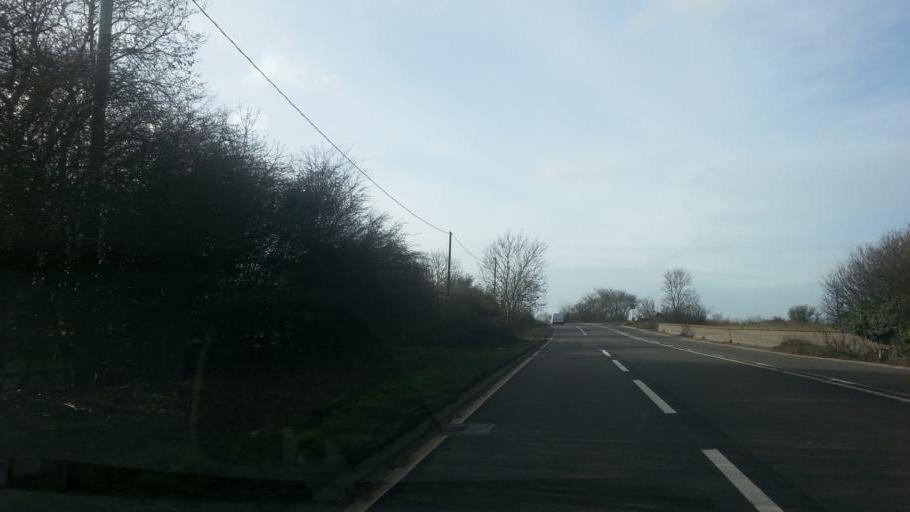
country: GB
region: England
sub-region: District of Rutland
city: Ridlington
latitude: 52.5945
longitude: -0.8305
